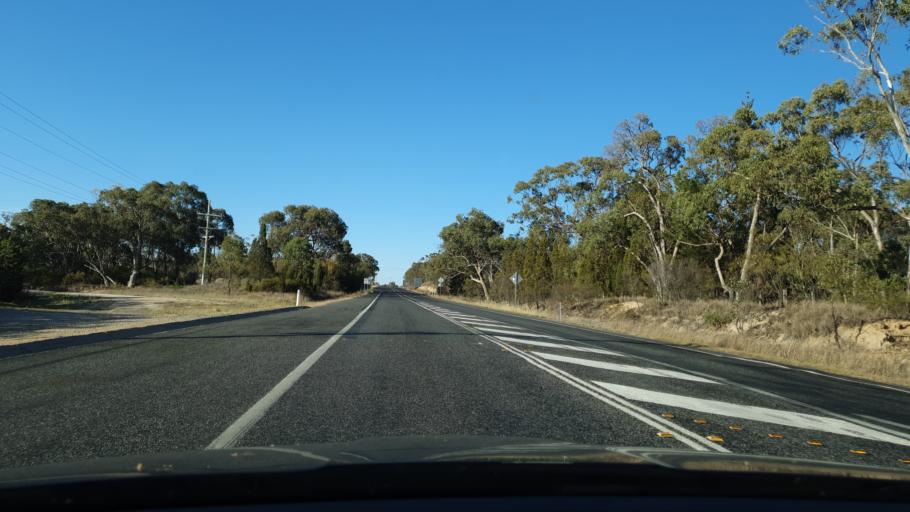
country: AU
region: Queensland
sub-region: Southern Downs
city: Stanthorpe
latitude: -28.6974
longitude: 151.9062
